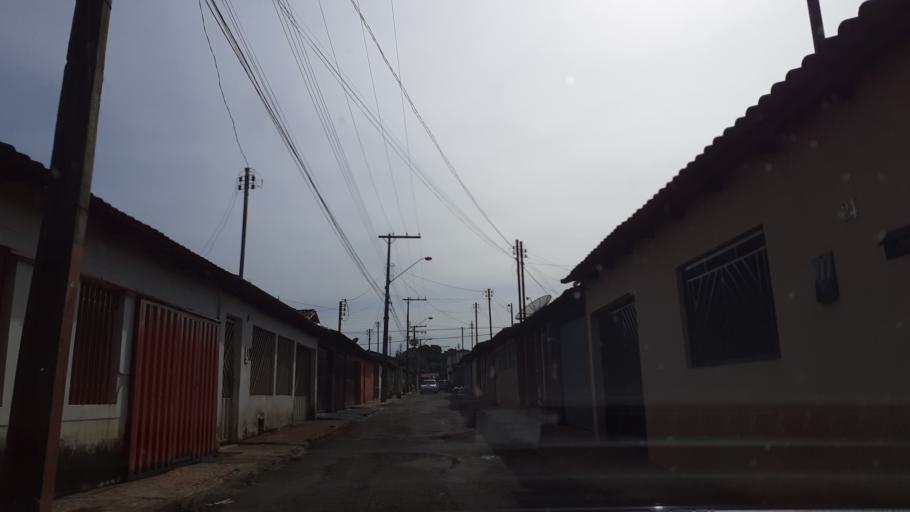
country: BR
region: Goias
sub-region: Itumbiara
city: Itumbiara
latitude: -18.4162
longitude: -49.2397
